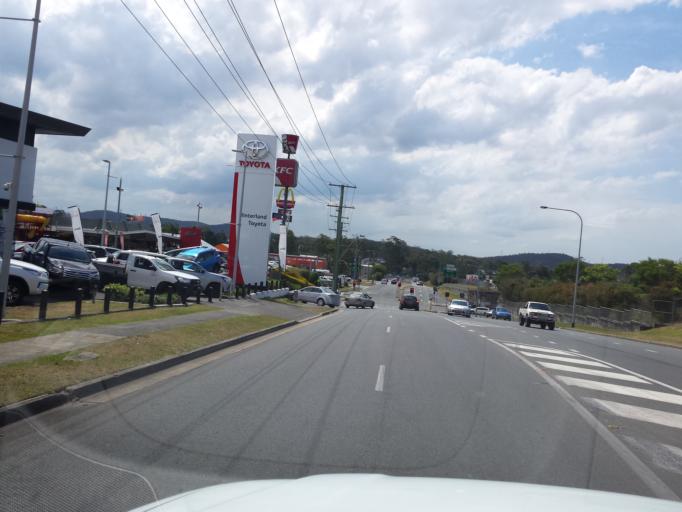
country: AU
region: Queensland
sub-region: Gold Coast
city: Nerang
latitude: -28.0084
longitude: 153.3430
